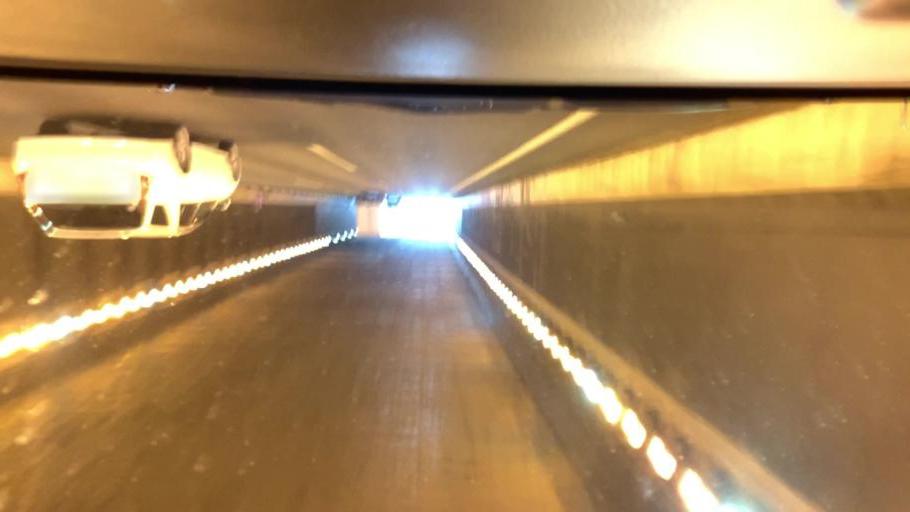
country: JP
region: Chiba
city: Nagareyama
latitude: 35.8516
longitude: 139.8762
